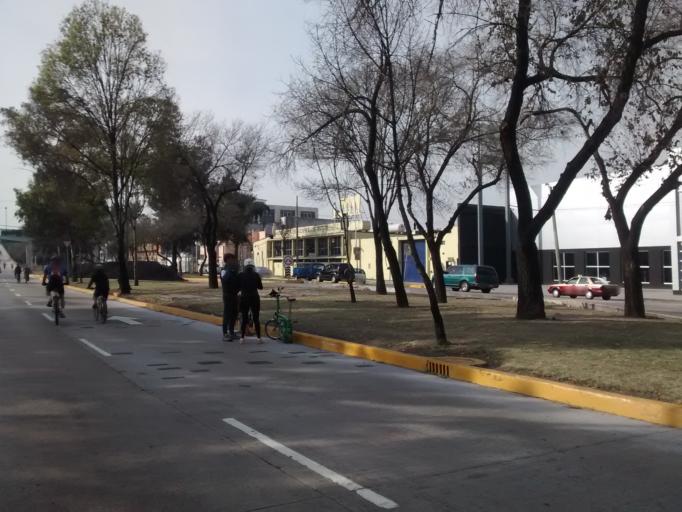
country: MX
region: Mexico City
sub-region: Iztacalco
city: Iztacalco
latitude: 19.3998
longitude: -99.0985
